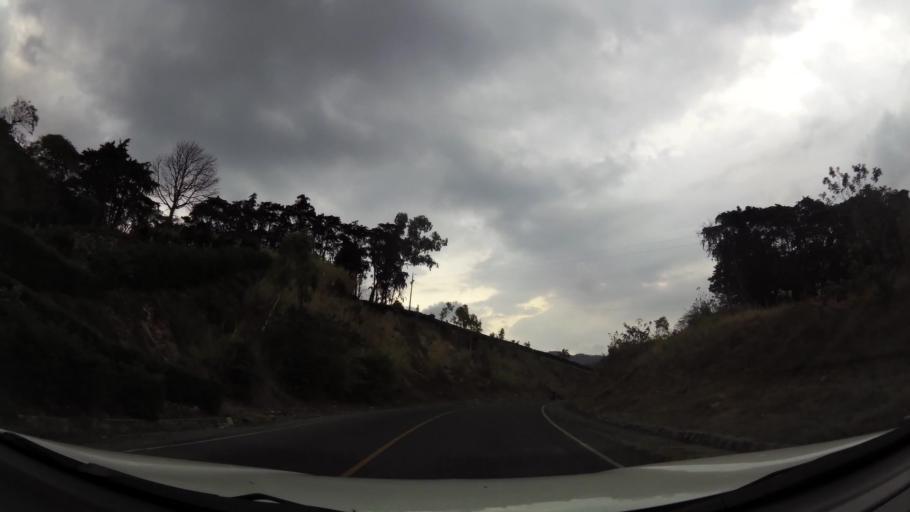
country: NI
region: Jinotega
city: Jinotega
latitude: 13.0689
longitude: -85.9871
